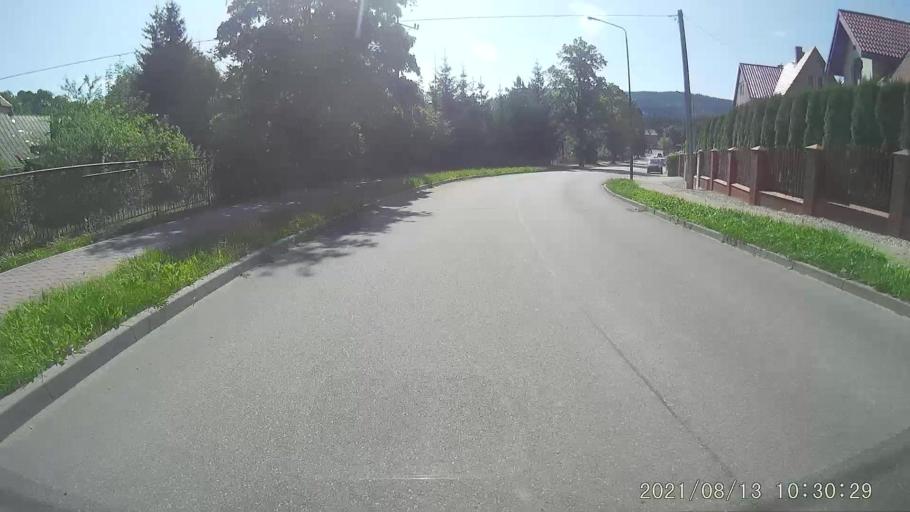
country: PL
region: Lower Silesian Voivodeship
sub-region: Powiat klodzki
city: Duszniki-Zdroj
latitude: 50.4078
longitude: 16.3845
